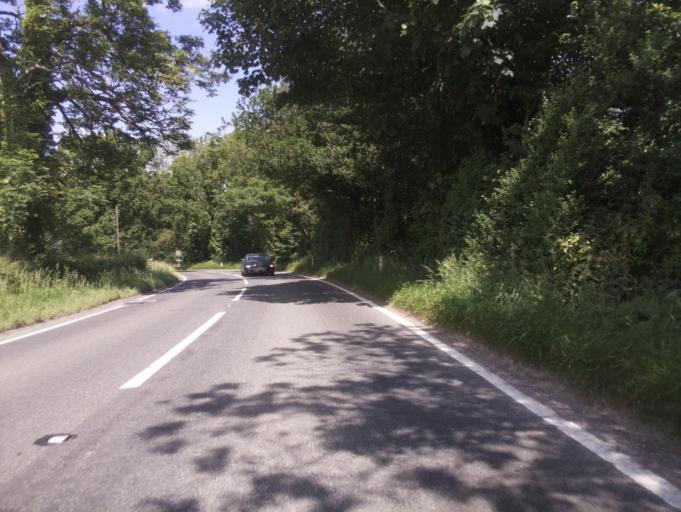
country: GB
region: England
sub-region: Somerset
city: Bruton
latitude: 51.0631
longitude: -2.4675
